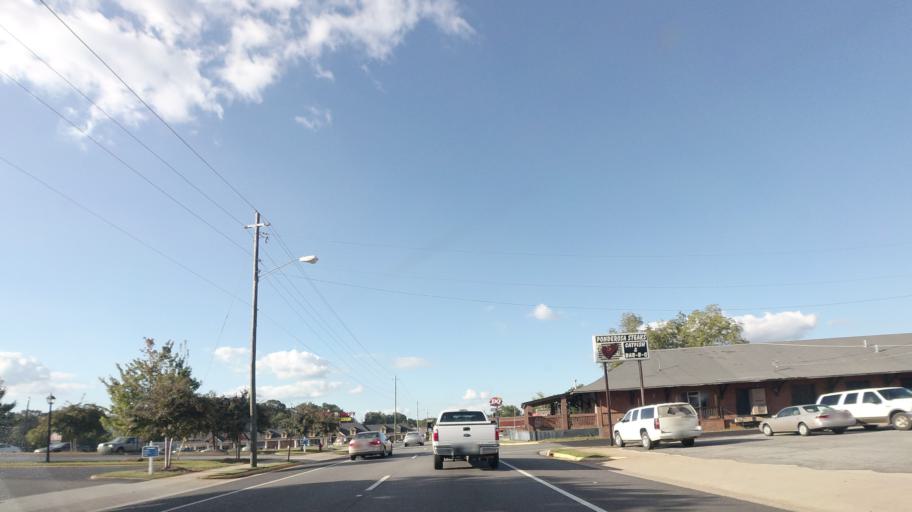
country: US
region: Georgia
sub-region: Upson County
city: Thomaston
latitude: 32.8899
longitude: -84.3262
